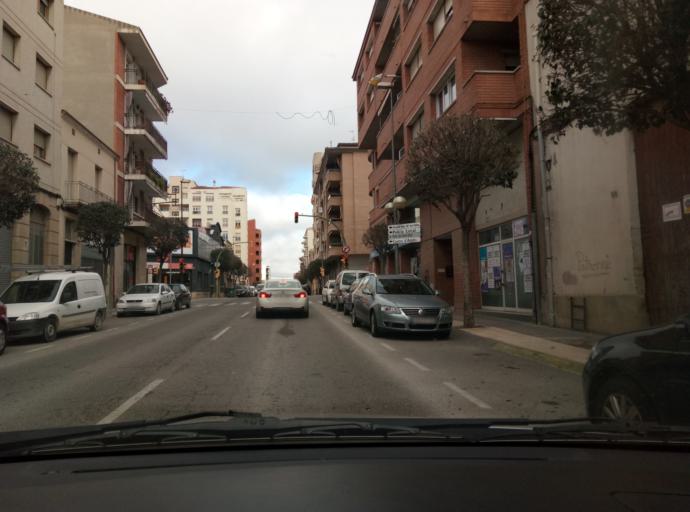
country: ES
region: Catalonia
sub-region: Provincia de Lleida
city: Tarrega
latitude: 41.6519
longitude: 1.1390
